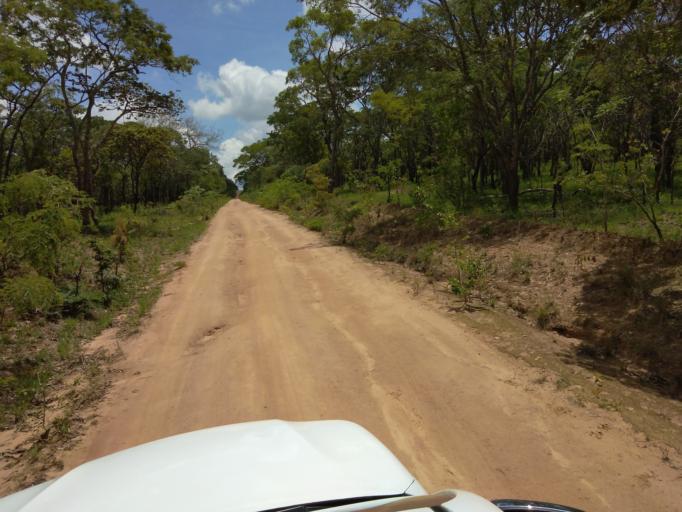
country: ZM
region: Central
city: Mkushi
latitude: -13.9002
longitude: 29.8607
